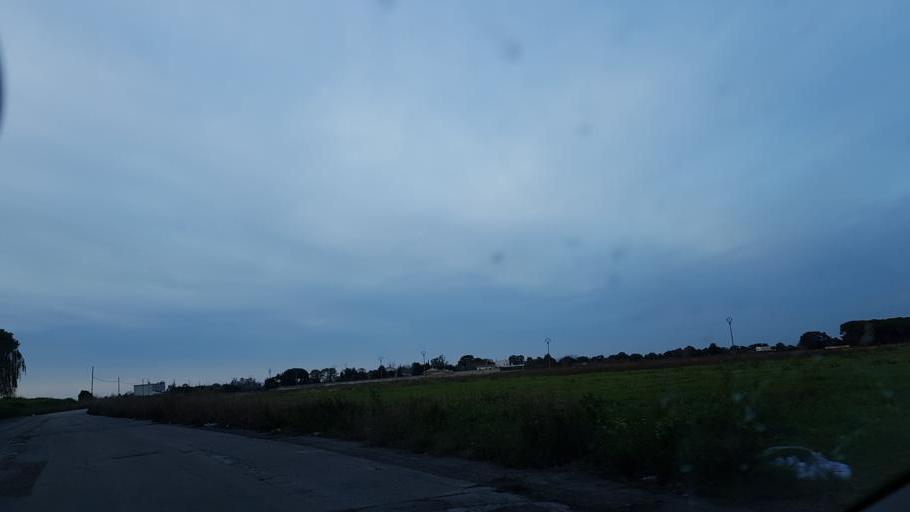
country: IT
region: Apulia
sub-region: Provincia di Brindisi
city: Brindisi
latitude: 40.6523
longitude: 17.9155
